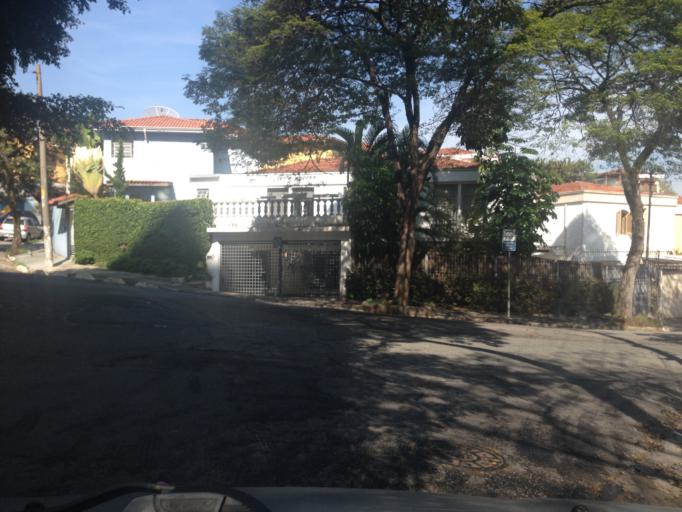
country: BR
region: Sao Paulo
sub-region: Sao Paulo
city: Sao Paulo
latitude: -23.5421
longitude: -46.7020
